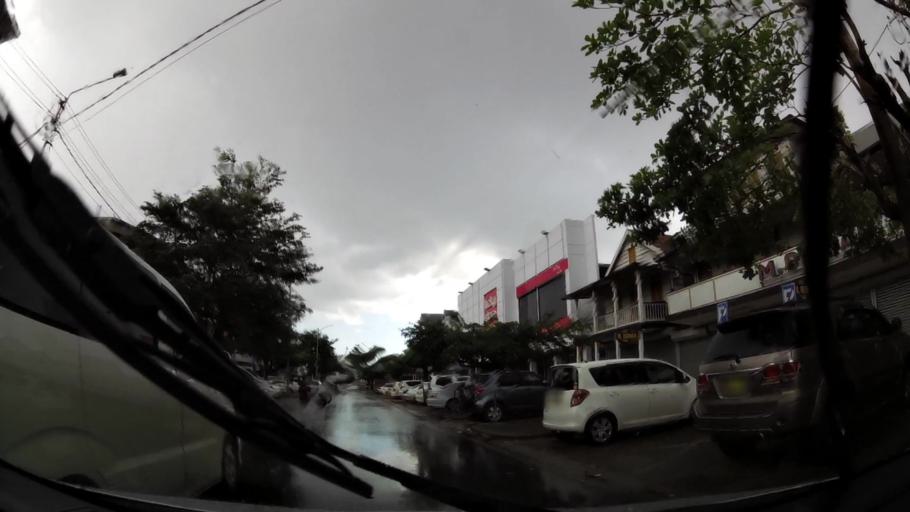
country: SR
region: Paramaribo
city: Paramaribo
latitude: 5.8259
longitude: -55.1589
